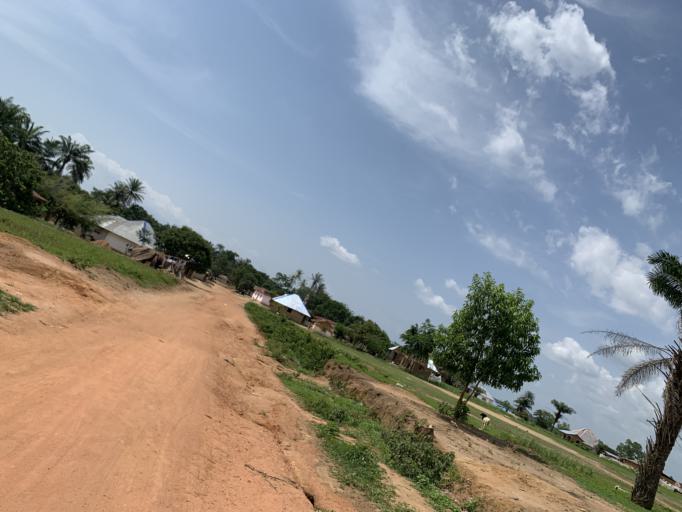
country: SL
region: Western Area
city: Waterloo
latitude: 8.3643
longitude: -13.0424
